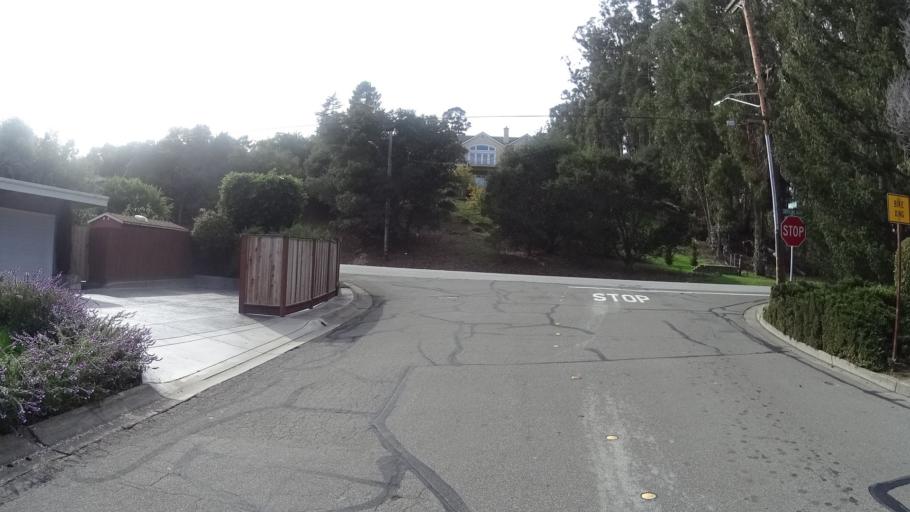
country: US
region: California
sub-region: San Mateo County
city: Hillsborough
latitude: 37.5758
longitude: -122.3978
